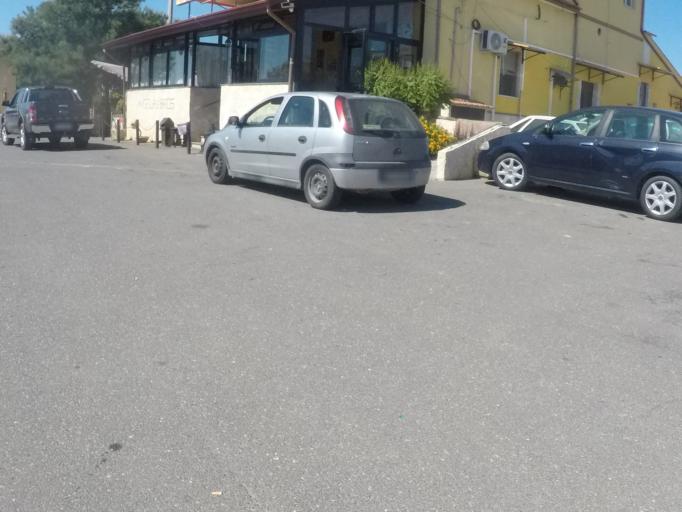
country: IT
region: Sicily
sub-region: Catania
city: Motta Sant'Anastasia
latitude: 37.4635
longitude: 14.9350
